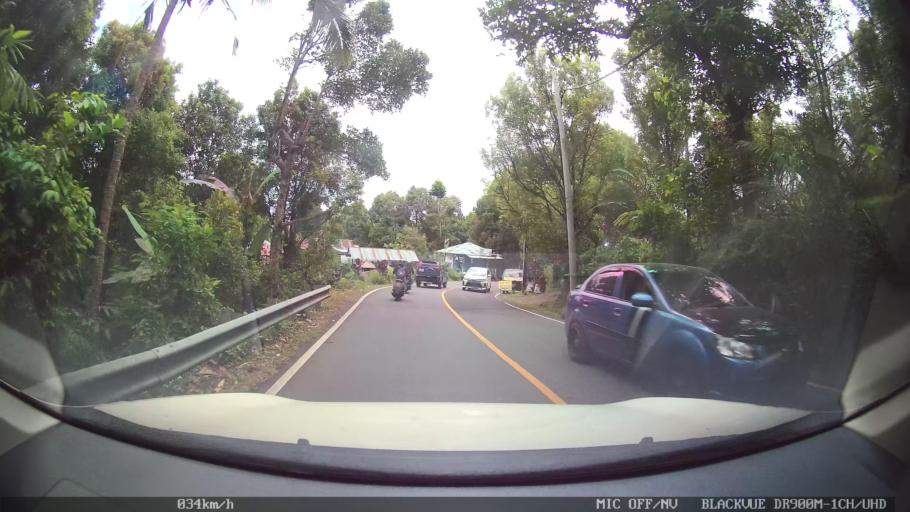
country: ID
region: Bali
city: Banjar Ambengan
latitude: -8.1940
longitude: 115.1392
